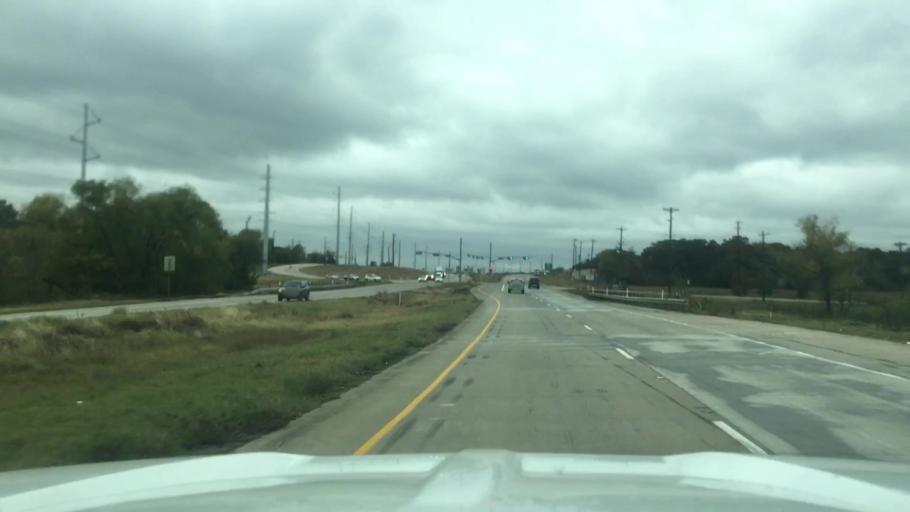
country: US
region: Texas
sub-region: Denton County
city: Denton
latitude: 33.2472
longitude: -97.0933
